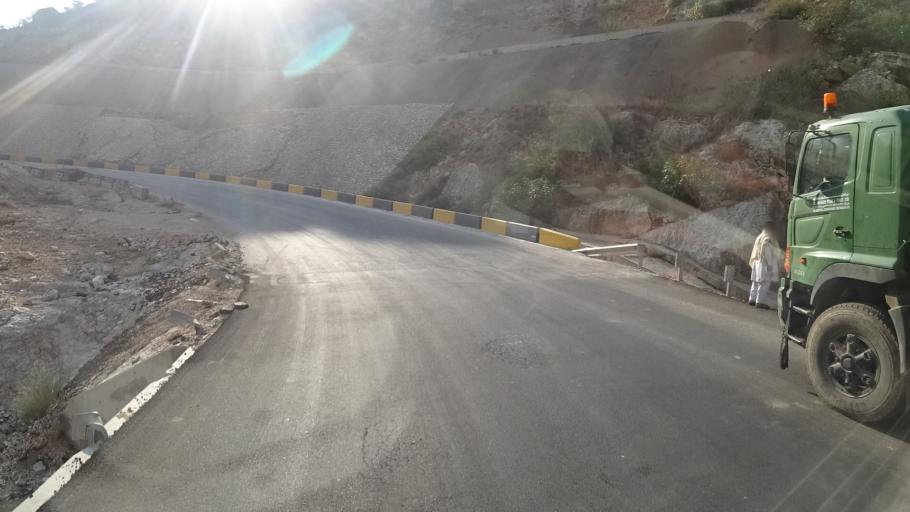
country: YE
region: Al Mahrah
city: Hawf
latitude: 16.7483
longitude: 53.2242
